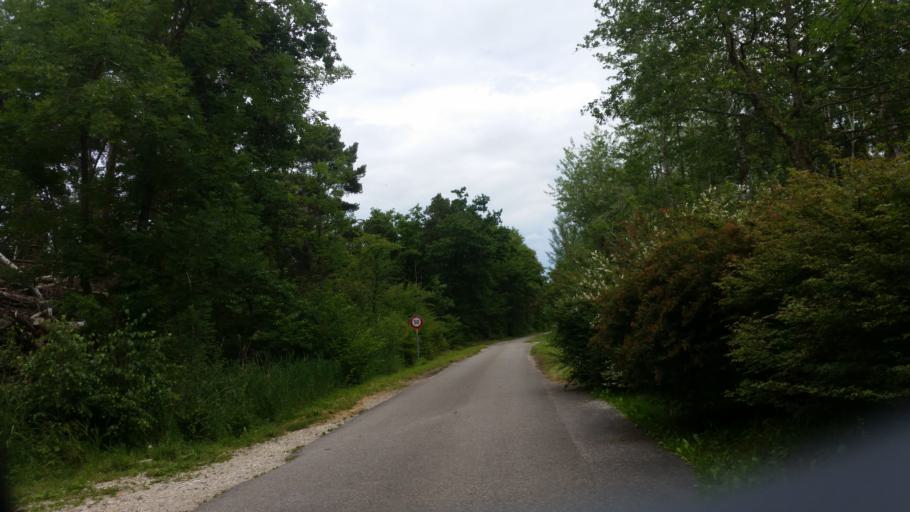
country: CH
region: Fribourg
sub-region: Broye District
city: Estavayer-le-Lac
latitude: 46.8418
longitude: 6.8259
